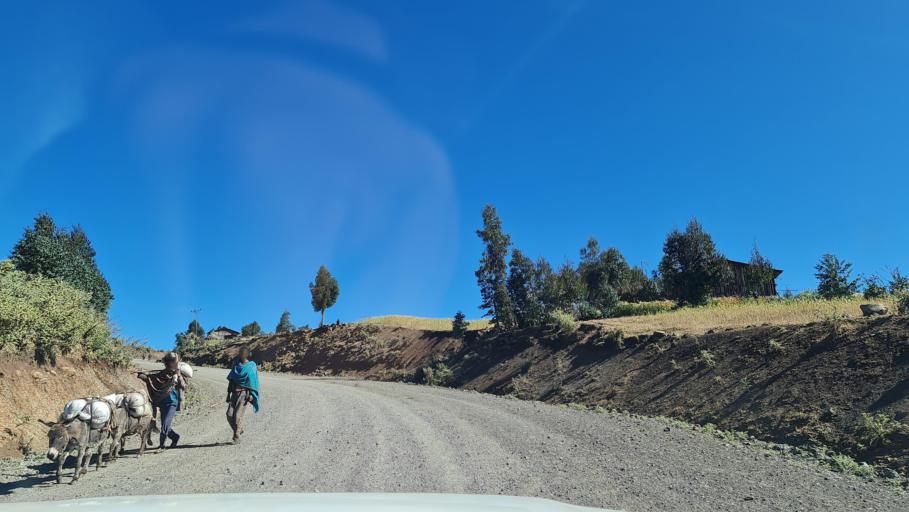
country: ET
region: Amhara
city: Debark'
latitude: 13.1166
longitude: 38.1544
